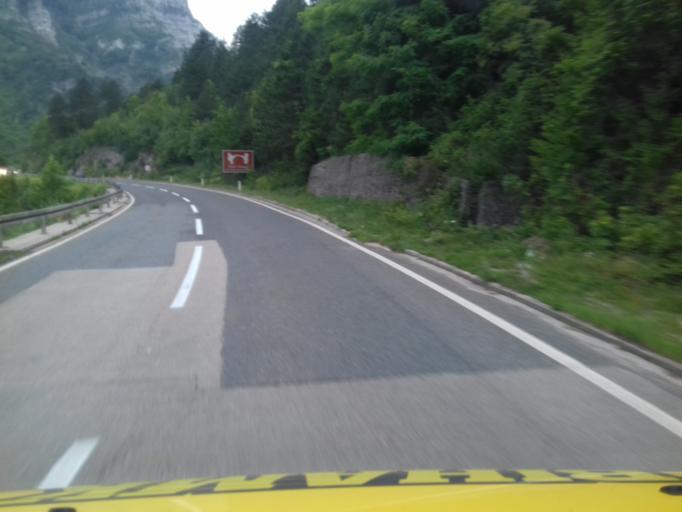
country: BA
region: Federation of Bosnia and Herzegovina
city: Jablanica
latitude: 43.6262
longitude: 17.7509
